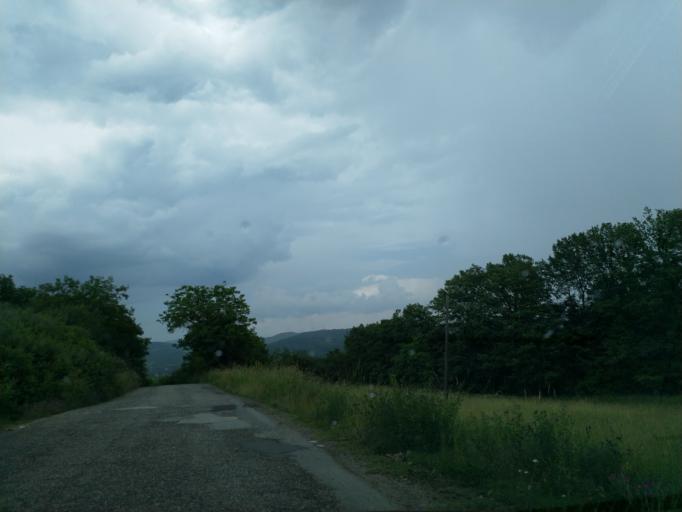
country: RS
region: Central Serbia
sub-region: Borski Okrug
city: Bor
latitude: 43.9926
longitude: 21.9776
